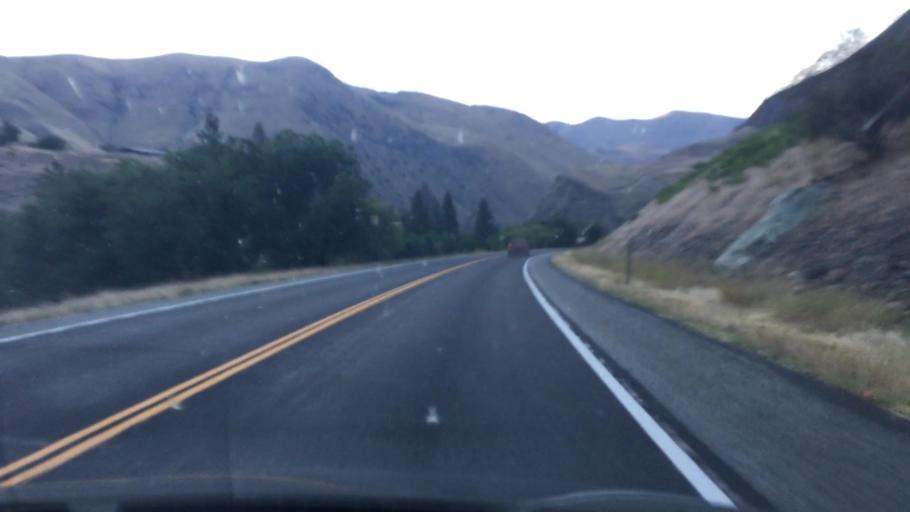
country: US
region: Idaho
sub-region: Valley County
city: McCall
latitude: 45.3479
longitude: -116.3550
